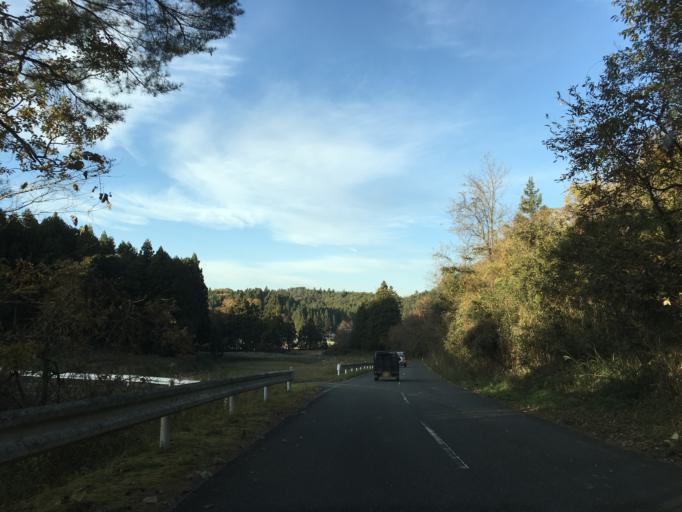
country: JP
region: Iwate
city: Ichinoseki
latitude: 38.8054
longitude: 141.1695
